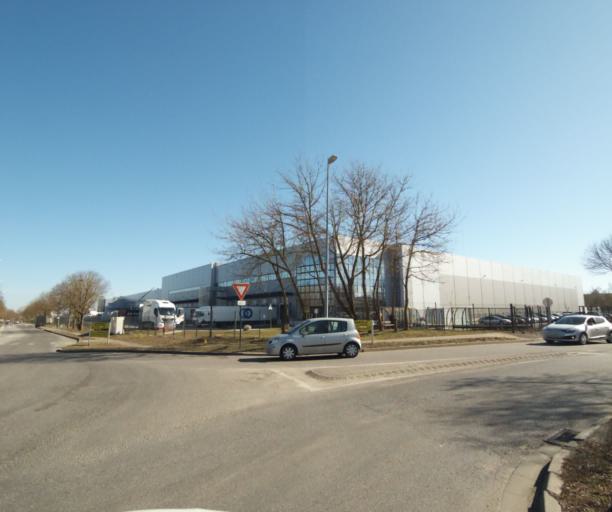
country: FR
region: Lorraine
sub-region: Departement de Meurthe-et-Moselle
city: Fleville-devant-Nancy
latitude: 48.6100
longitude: 6.1918
